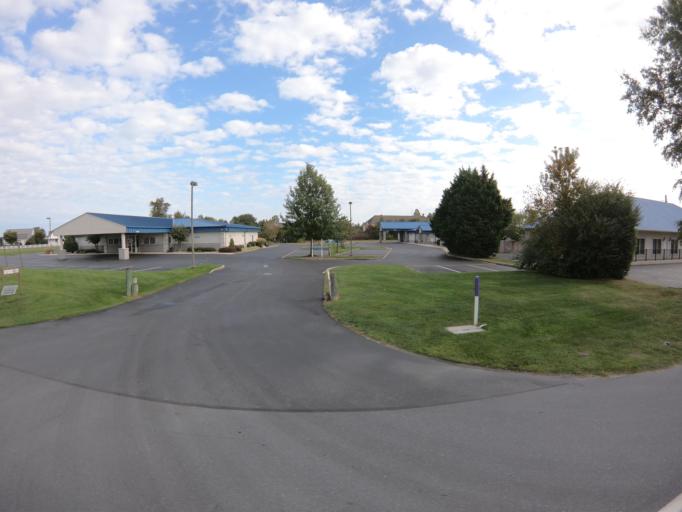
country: US
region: Delaware
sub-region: Sussex County
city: Lewes
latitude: 38.7522
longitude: -75.1656
